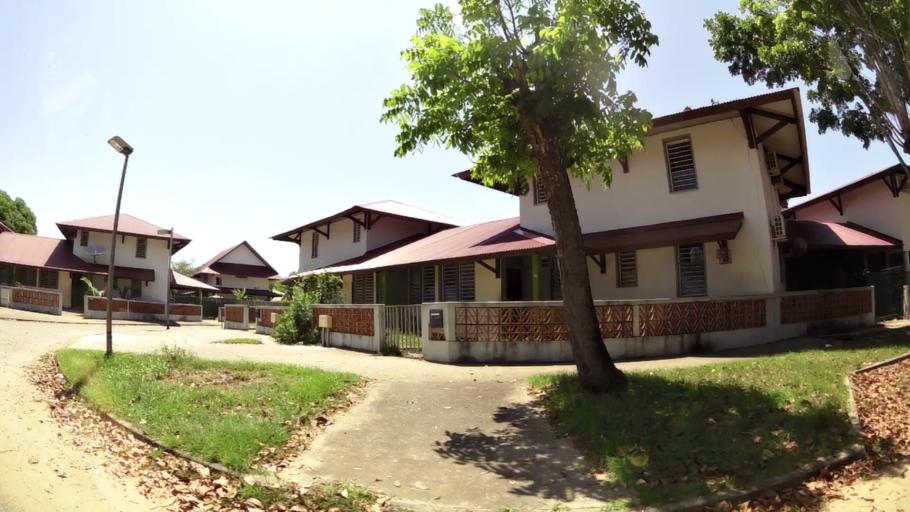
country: GF
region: Guyane
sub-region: Guyane
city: Kourou
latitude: 5.1750
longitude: -52.6475
